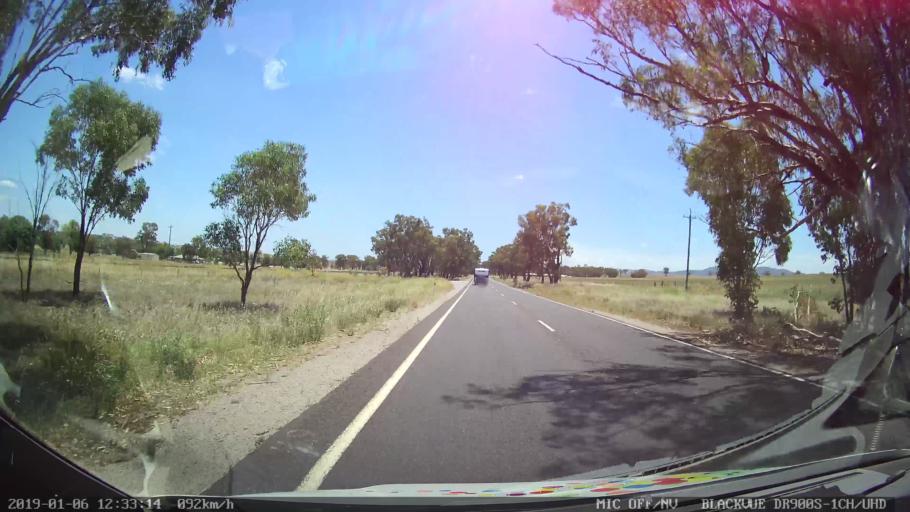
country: AU
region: New South Wales
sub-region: Tamworth Municipality
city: Phillip
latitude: -31.1435
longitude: 150.8775
